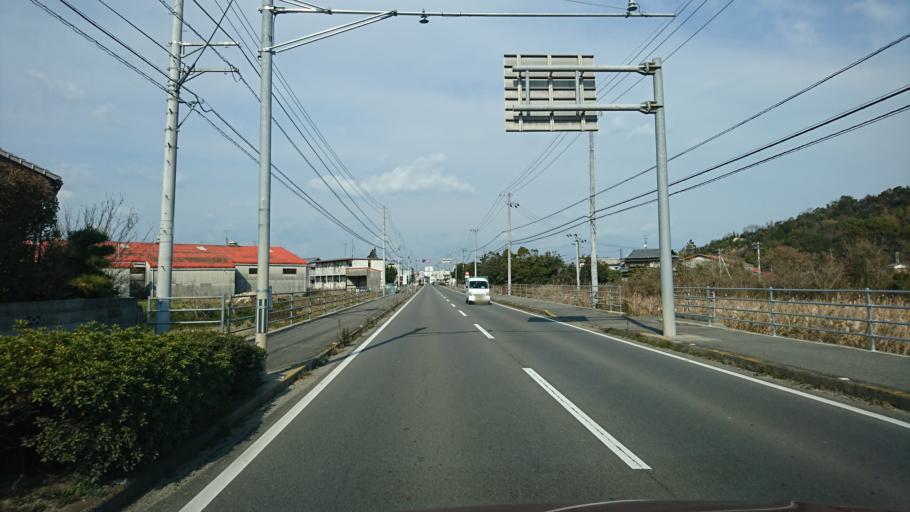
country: JP
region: Ehime
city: Saijo
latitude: 34.0097
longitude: 133.0386
